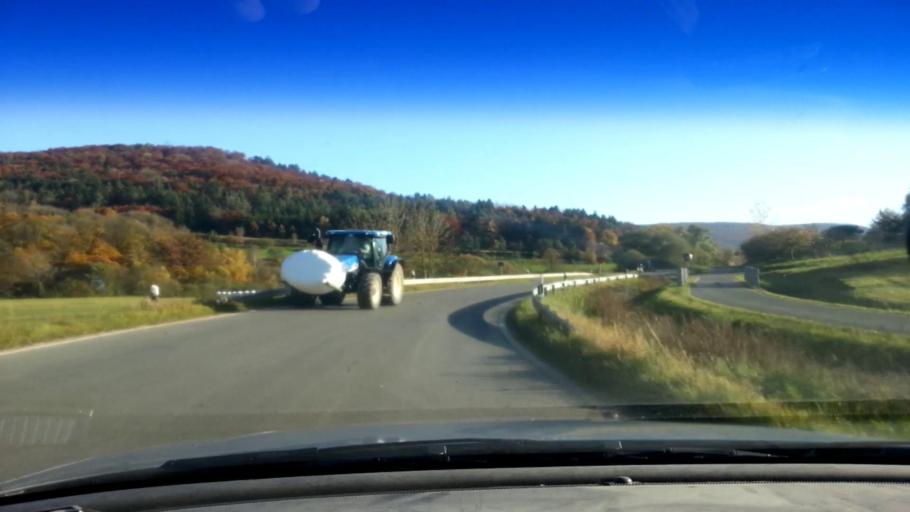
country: DE
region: Bavaria
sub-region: Upper Franconia
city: Poxdorf
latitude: 49.8902
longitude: 11.1271
